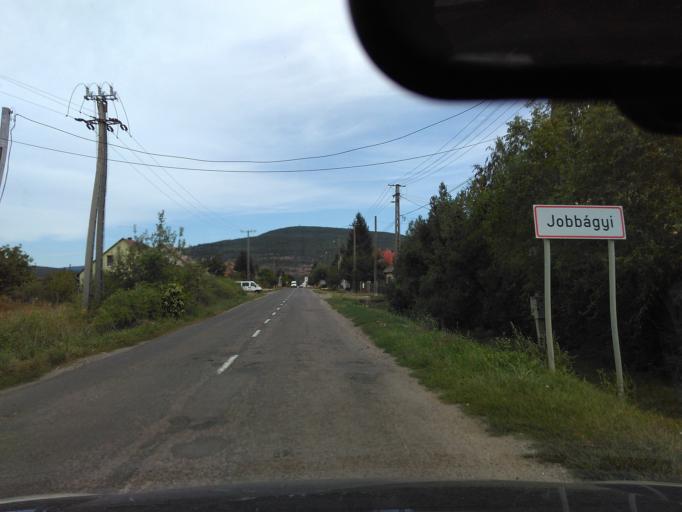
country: HU
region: Nograd
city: Jobbagyi
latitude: 47.8294
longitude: 19.6655
